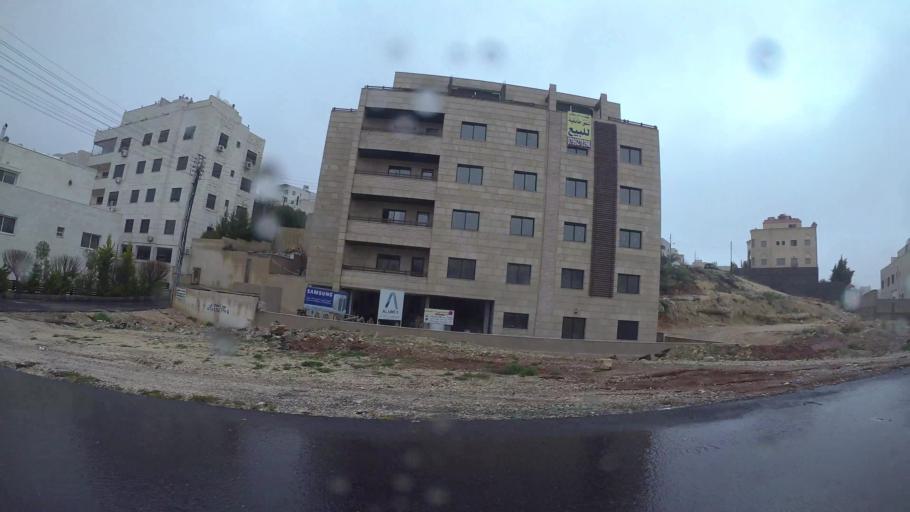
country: JO
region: Amman
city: Al Jubayhah
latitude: 32.0050
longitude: 35.8223
